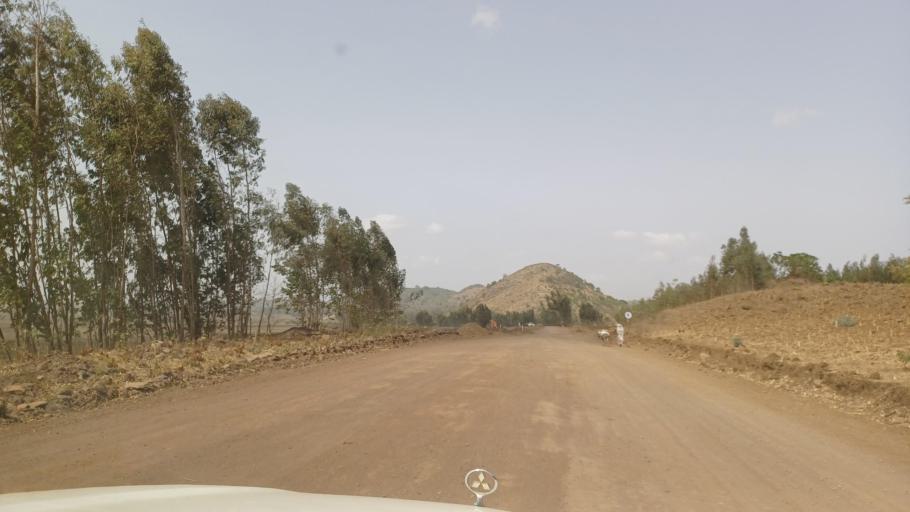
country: ET
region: Amhara
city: Bahir Dar
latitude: 11.8452
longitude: 37.0039
